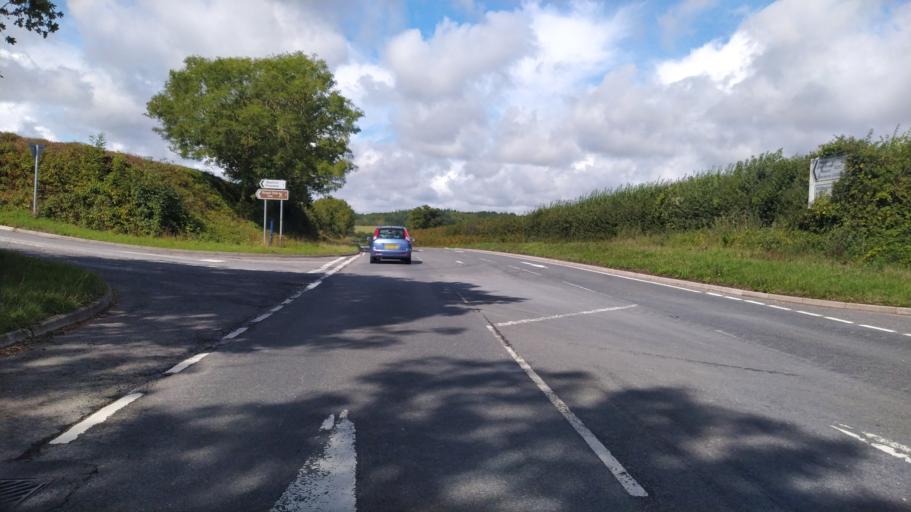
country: GB
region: England
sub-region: Dorset
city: Manston
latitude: 50.9114
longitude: -2.2692
